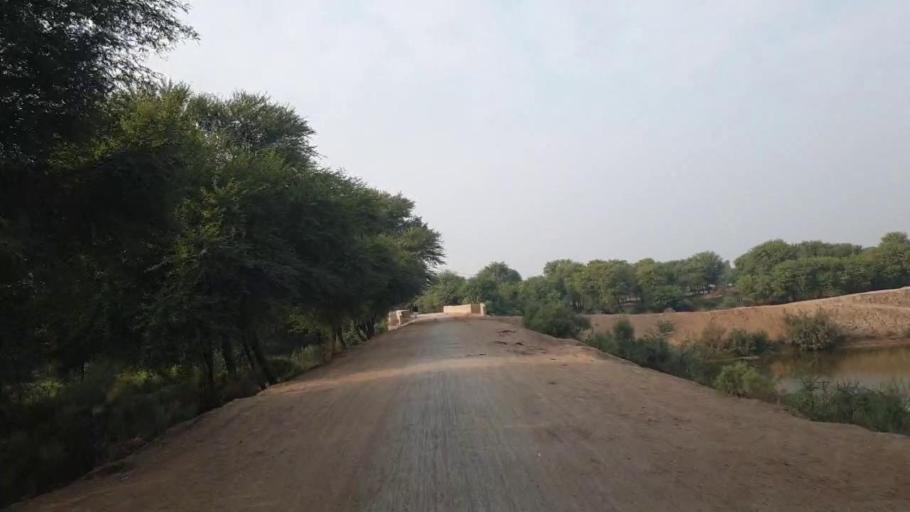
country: PK
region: Sindh
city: Sann
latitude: 26.1411
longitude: 68.0494
